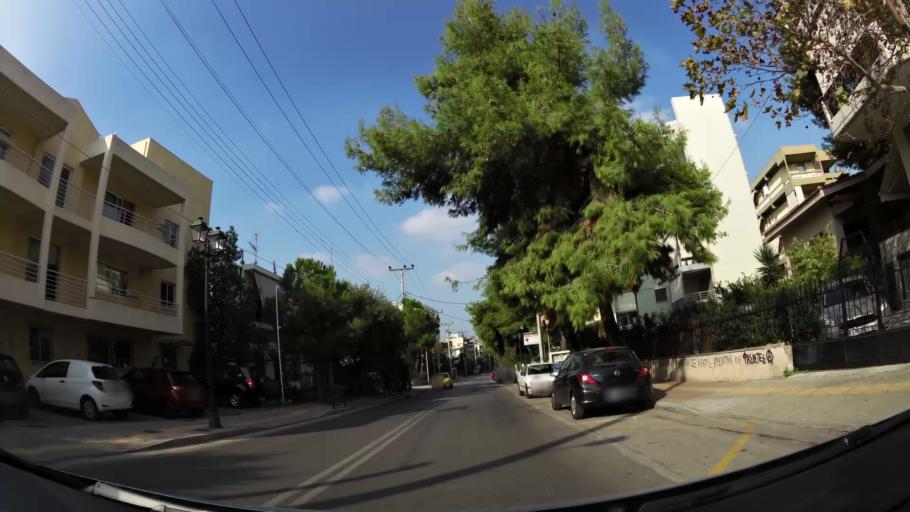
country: GR
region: Attica
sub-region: Nomarchia Athinas
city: Cholargos
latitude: 38.0081
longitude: 23.8123
